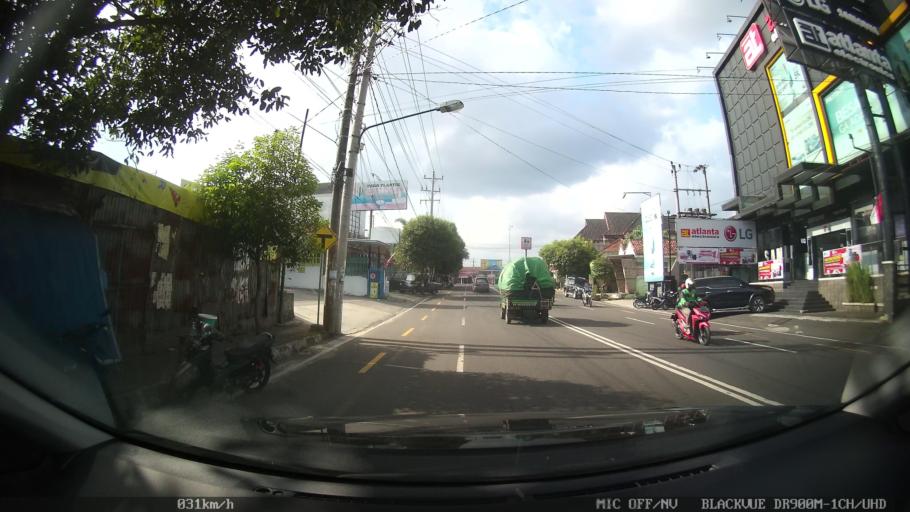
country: ID
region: Daerah Istimewa Yogyakarta
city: Yogyakarta
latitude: -7.7831
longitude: 110.3525
